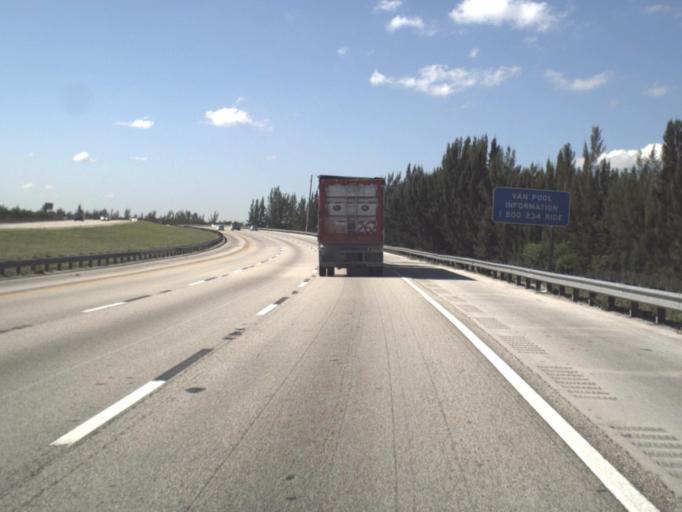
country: US
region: Florida
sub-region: Miami-Dade County
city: Palm Springs North
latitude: 25.9306
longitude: -80.3736
